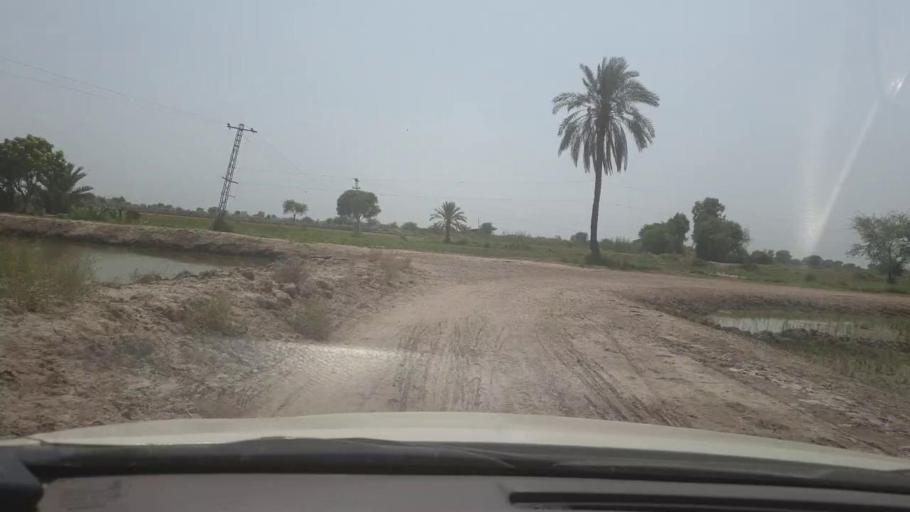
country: PK
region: Sindh
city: Shikarpur
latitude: 27.9617
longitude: 68.5876
